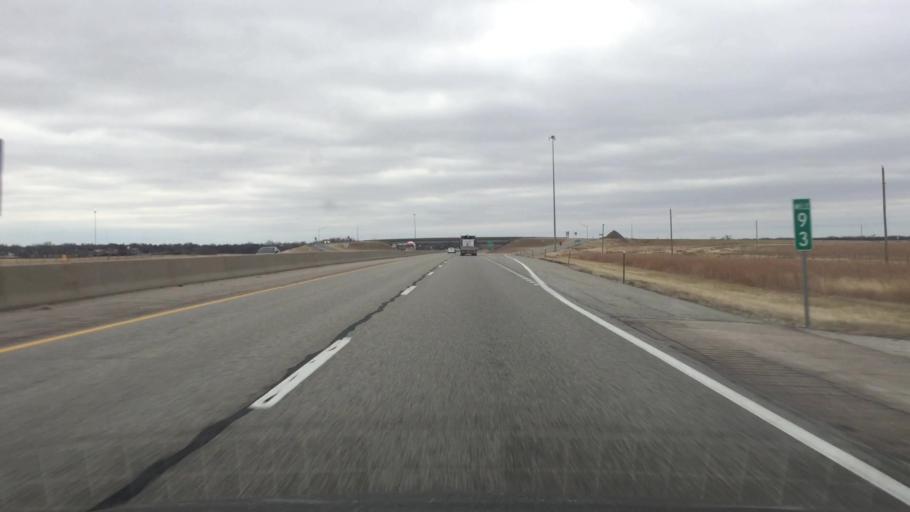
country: US
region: Kansas
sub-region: Chase County
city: Cottonwood Falls
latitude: 38.0538
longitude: -96.6301
